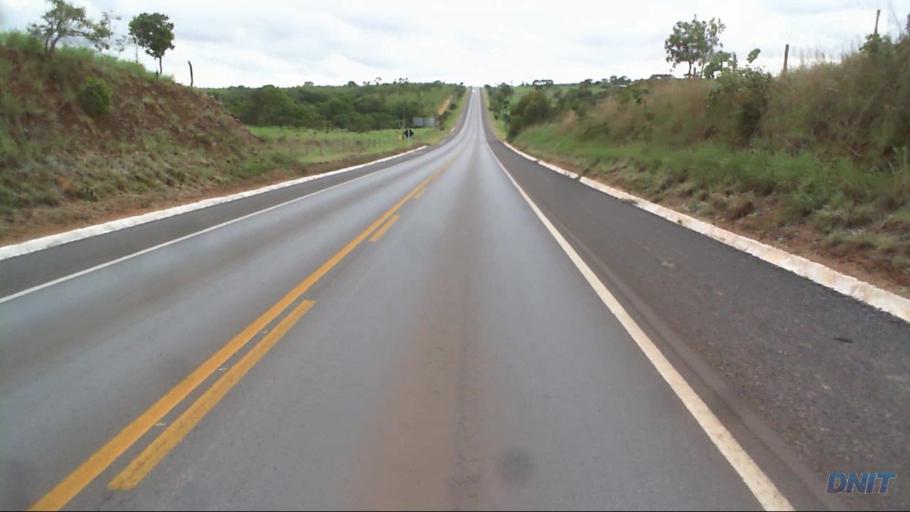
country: BR
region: Goias
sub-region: Barro Alto
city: Barro Alto
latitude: -15.2101
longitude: -48.6695
